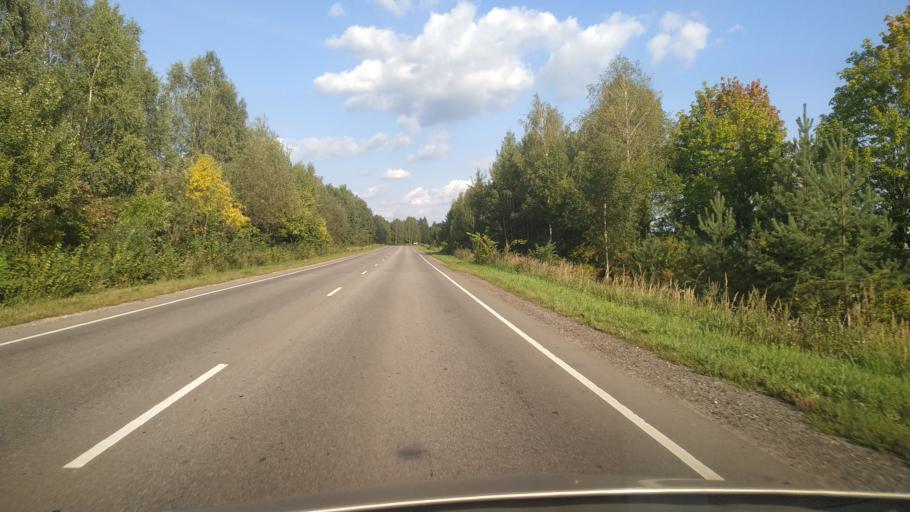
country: RU
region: Moskovskaya
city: Vereya
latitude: 55.7075
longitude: 39.1389
